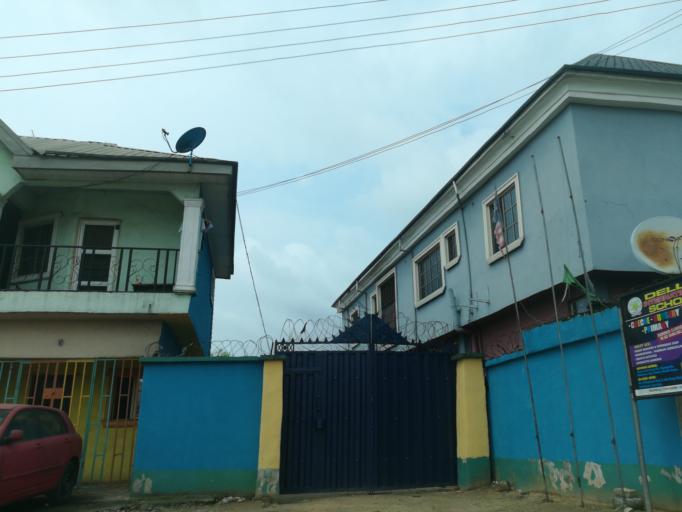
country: NG
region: Rivers
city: Port Harcourt
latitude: 4.8995
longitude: 6.9913
